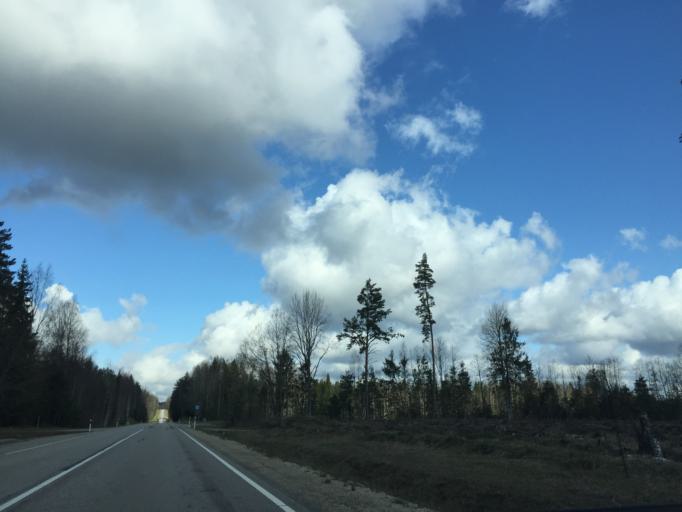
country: LV
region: Apes Novads
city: Ape
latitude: 57.5104
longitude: 26.7757
